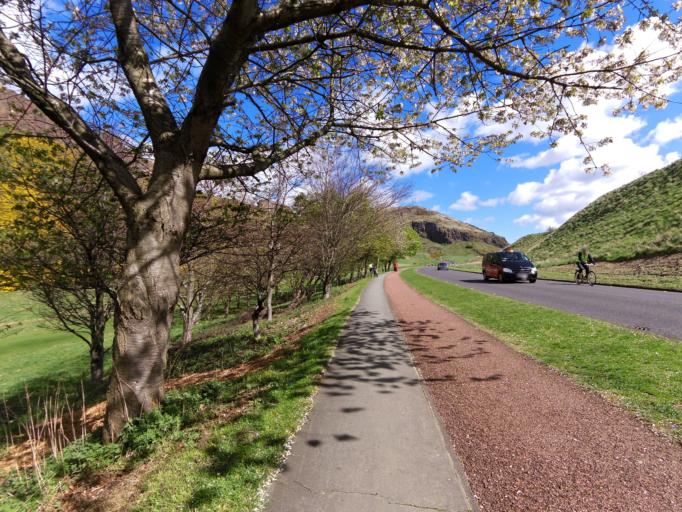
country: GB
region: Scotland
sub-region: Edinburgh
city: Edinburgh
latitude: 55.9430
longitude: -3.1735
